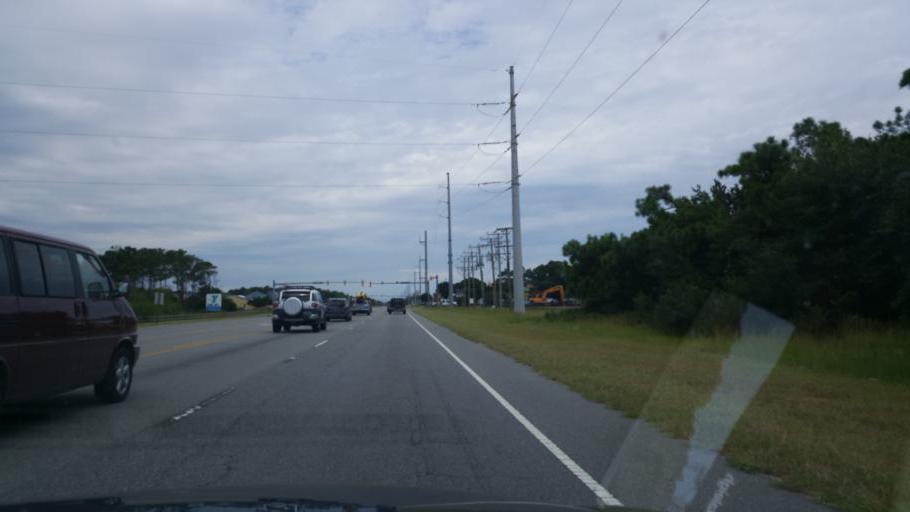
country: US
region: North Carolina
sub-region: Dare County
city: Nags Head
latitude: 35.9761
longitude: -75.6401
